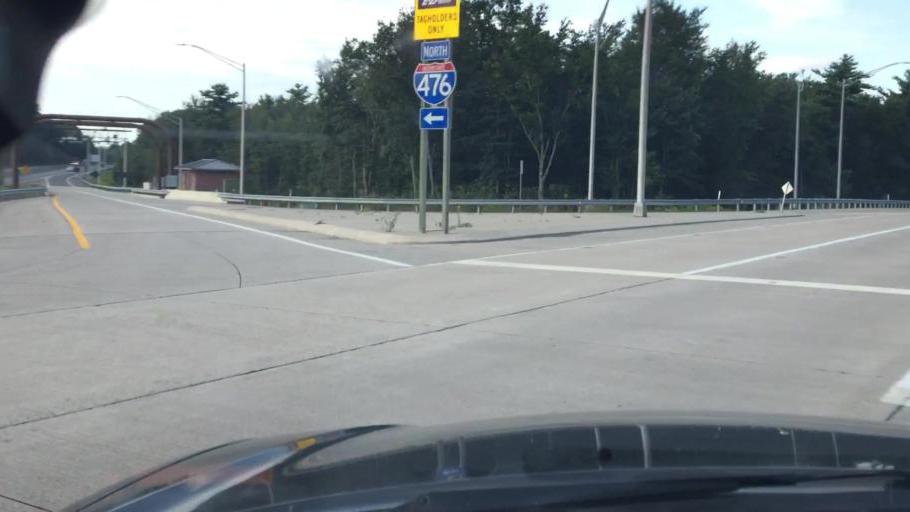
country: US
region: Pennsylvania
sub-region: Carbon County
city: Towamensing Trails
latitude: 40.9841
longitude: -75.6294
